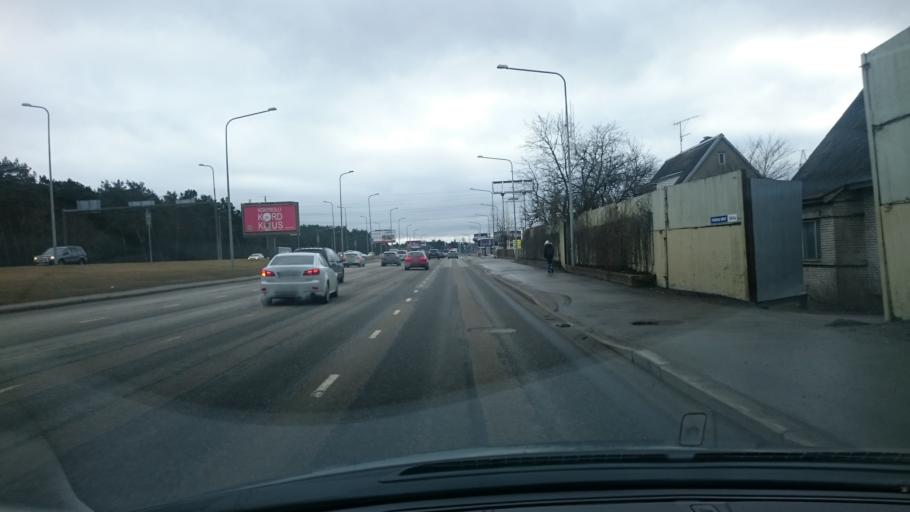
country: EE
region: Harju
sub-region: Tallinna linn
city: Tallinn
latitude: 59.3991
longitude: 24.7268
